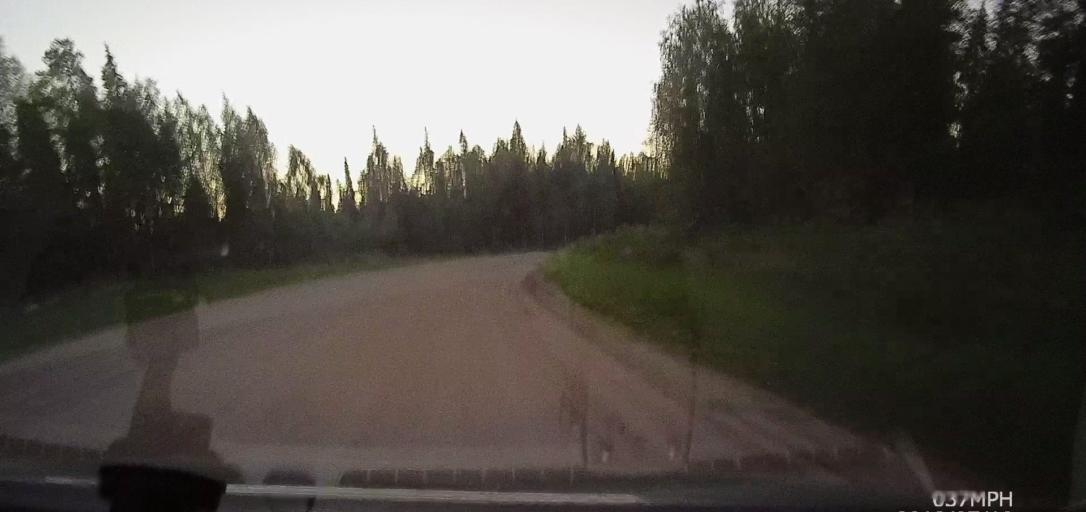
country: RU
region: Arkhangelskaya
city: Pinega
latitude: 64.4301
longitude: 43.1272
